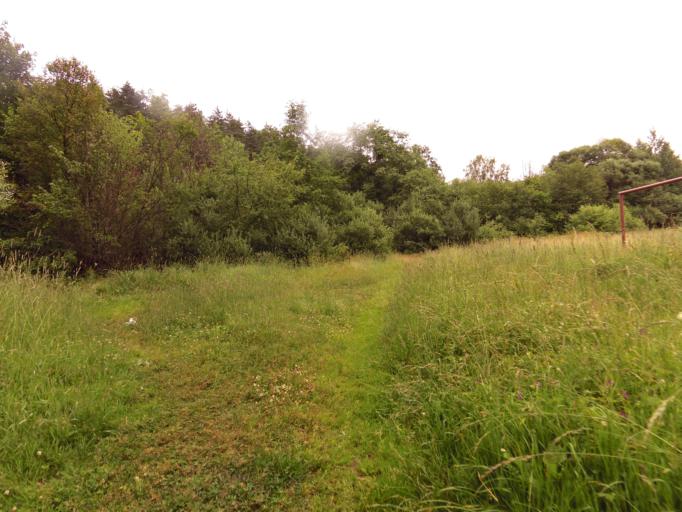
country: LT
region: Vilnius County
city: Pilaite
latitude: 54.6989
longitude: 25.1872
